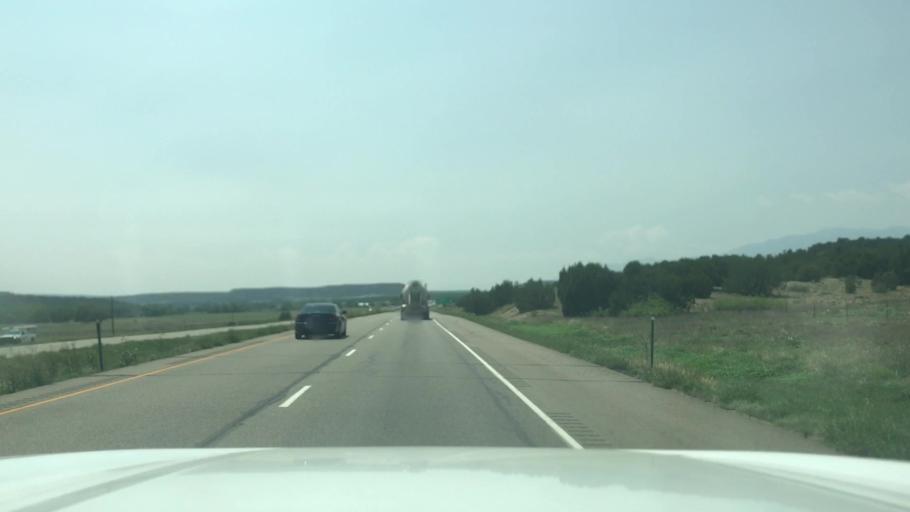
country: US
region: Colorado
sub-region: Pueblo County
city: Colorado City
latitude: 38.0062
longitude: -104.7513
